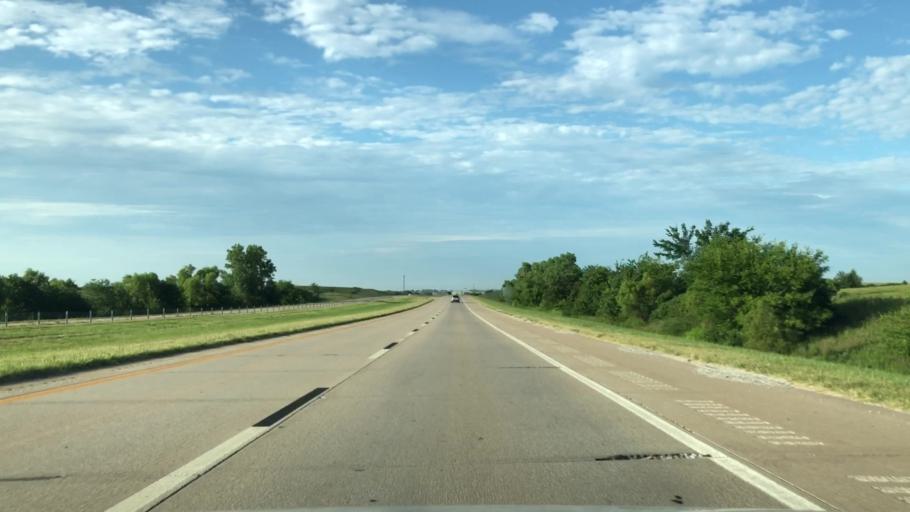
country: US
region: Oklahoma
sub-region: Osage County
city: Skiatook
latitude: 36.4121
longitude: -95.9207
